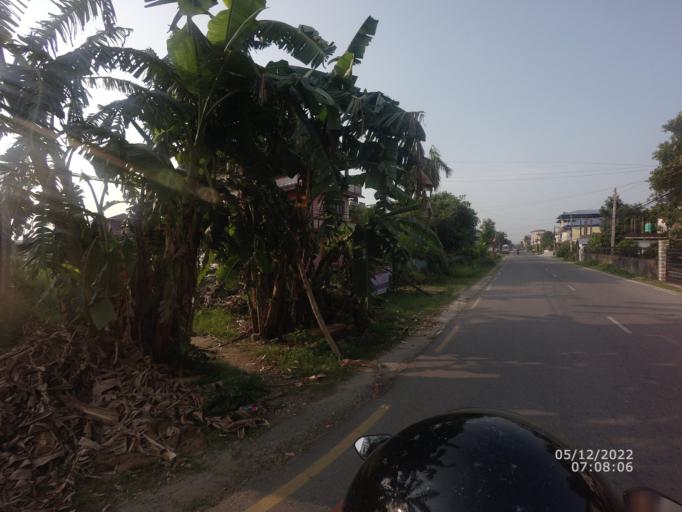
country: NP
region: Central Region
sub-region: Narayani Zone
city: Bharatpur
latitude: 27.6659
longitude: 84.4380
